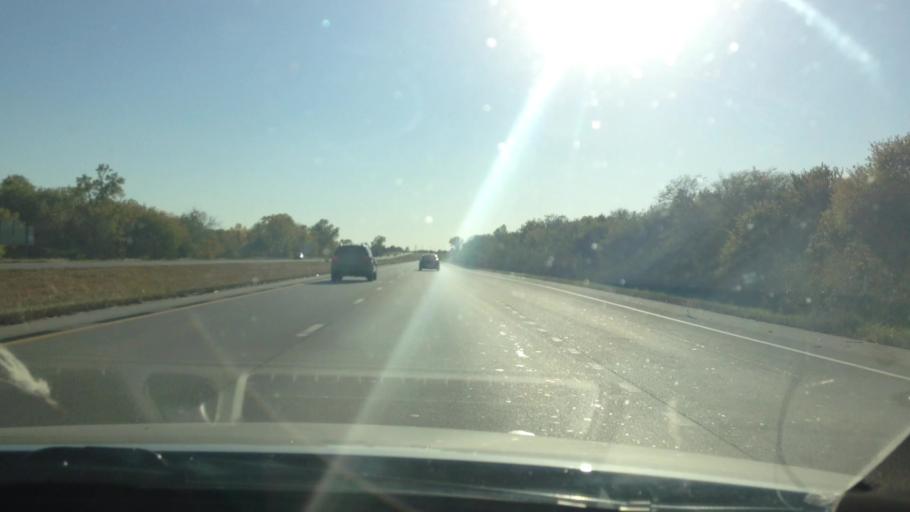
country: US
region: Kansas
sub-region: Johnson County
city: Gardner
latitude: 38.7790
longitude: -94.9317
